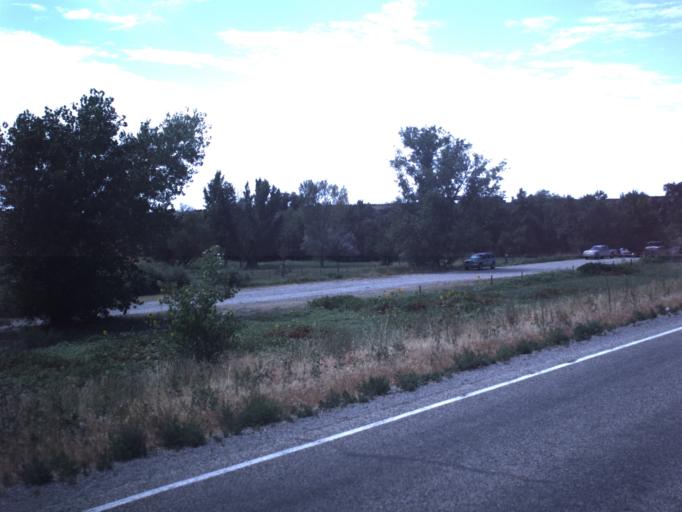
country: US
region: Utah
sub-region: Box Elder County
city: Elwood
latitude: 41.7136
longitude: -112.1150
